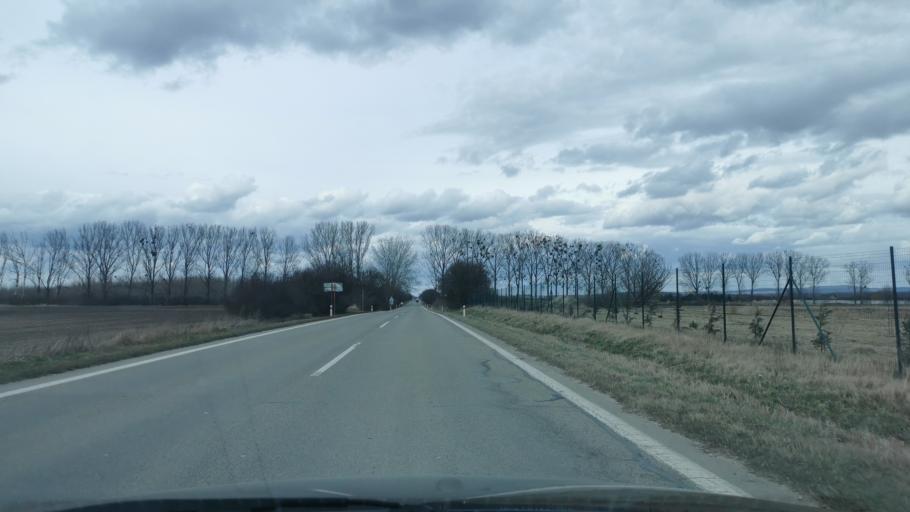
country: SK
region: Trnavsky
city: Gbely
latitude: 48.7739
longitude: 17.0974
